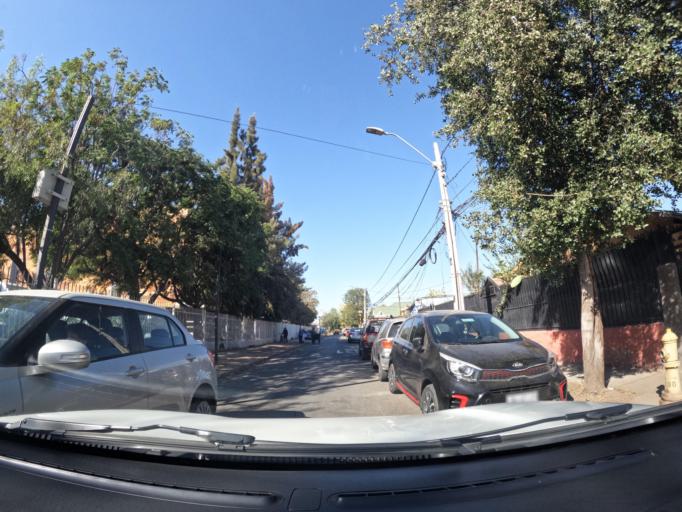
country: CL
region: Santiago Metropolitan
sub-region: Provincia de Santiago
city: Villa Presidente Frei, Nunoa, Santiago, Chile
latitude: -33.5028
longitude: -70.5785
